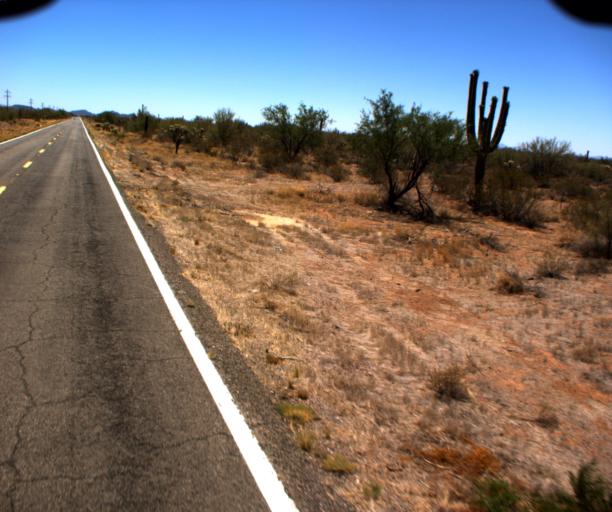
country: US
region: Arizona
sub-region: Pima County
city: Sells
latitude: 32.0679
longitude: -112.0397
